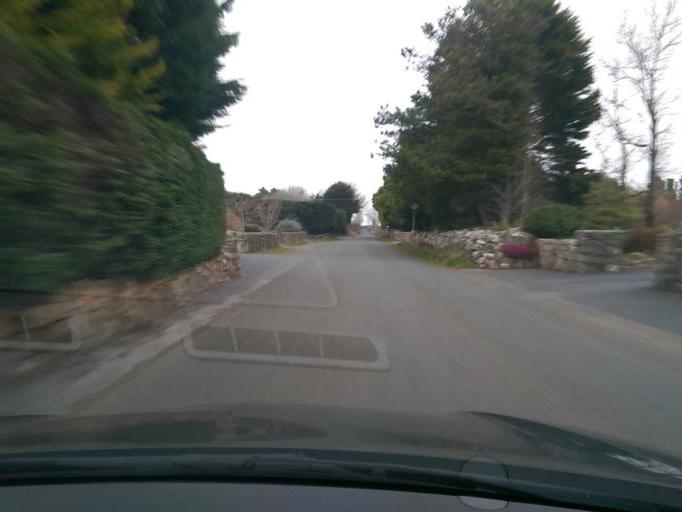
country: IE
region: Connaught
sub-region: County Galway
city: Bearna
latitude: 53.2569
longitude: -9.1535
